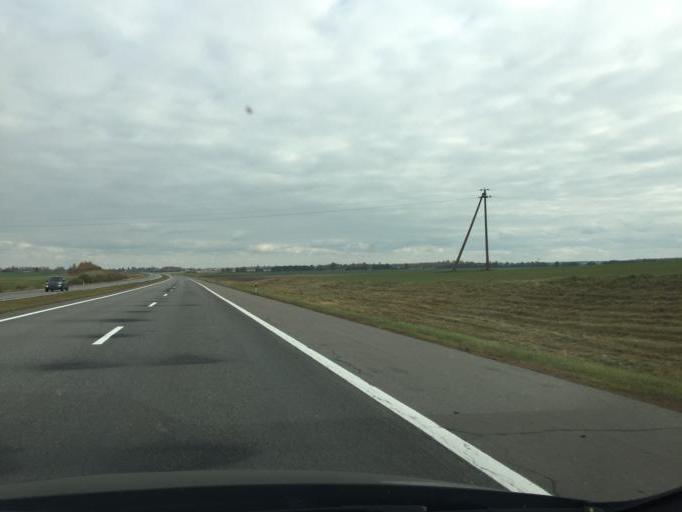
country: BY
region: Minsk
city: Stan'kava
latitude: 53.6762
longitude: 27.2146
